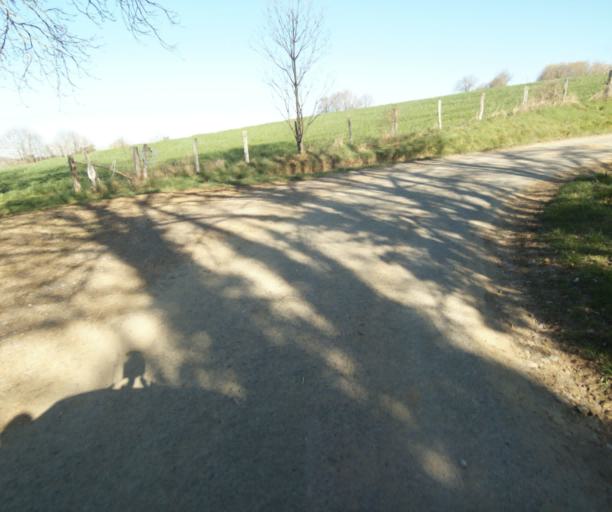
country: FR
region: Limousin
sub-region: Departement de la Correze
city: Seilhac
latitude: 45.3748
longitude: 1.7646
